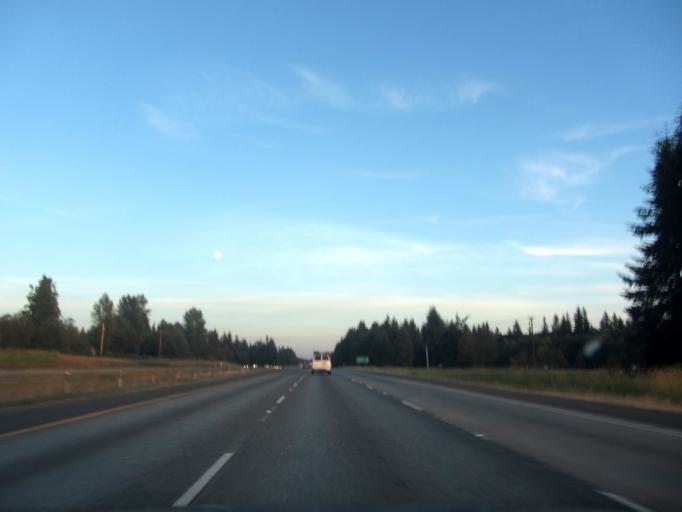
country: US
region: Washington
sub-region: Snohomish County
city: Stanwood
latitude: 48.2914
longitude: -122.2968
